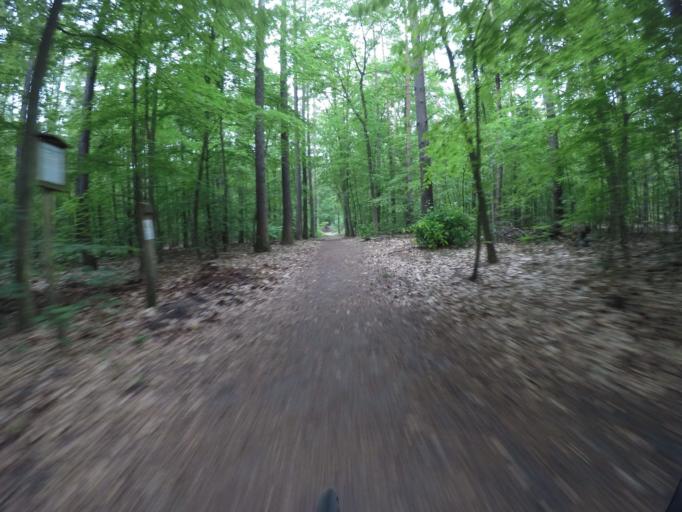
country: DE
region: Berlin
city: Frohnau
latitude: 52.6103
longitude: 13.2810
